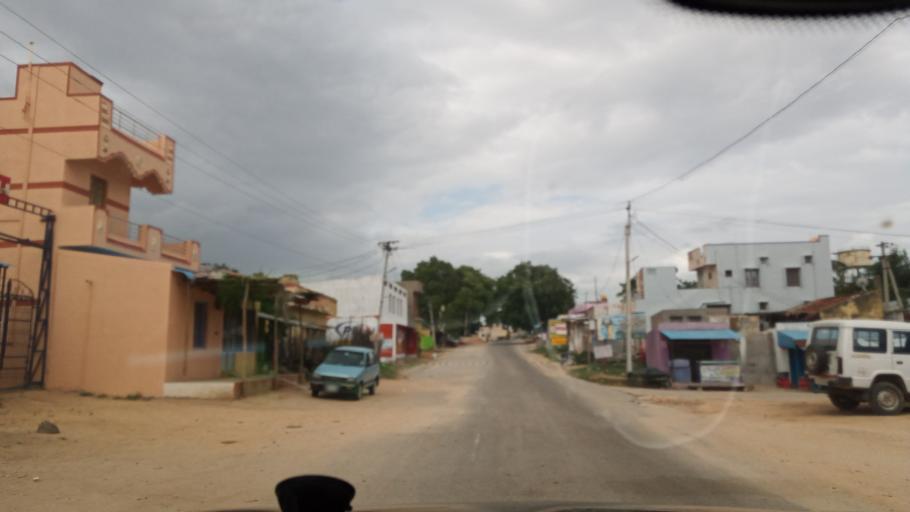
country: IN
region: Andhra Pradesh
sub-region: Chittoor
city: Palmaner
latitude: 13.1852
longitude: 78.8361
